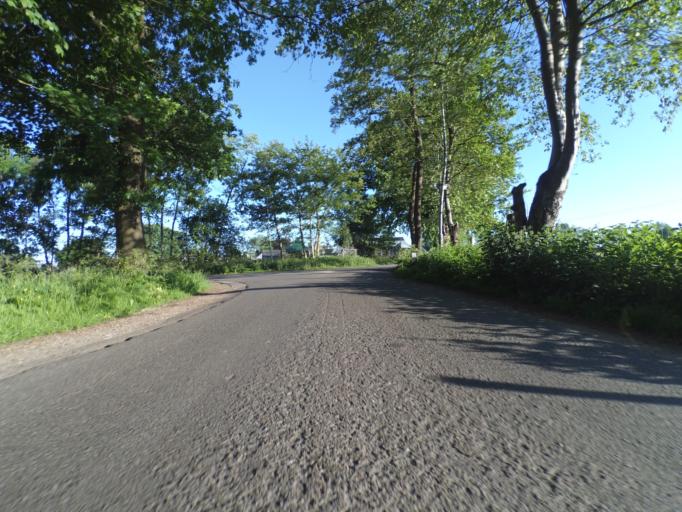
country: NL
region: Gelderland
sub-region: Gemeente Barneveld
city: Kootwijkerbroek
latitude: 52.1452
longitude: 5.6987
